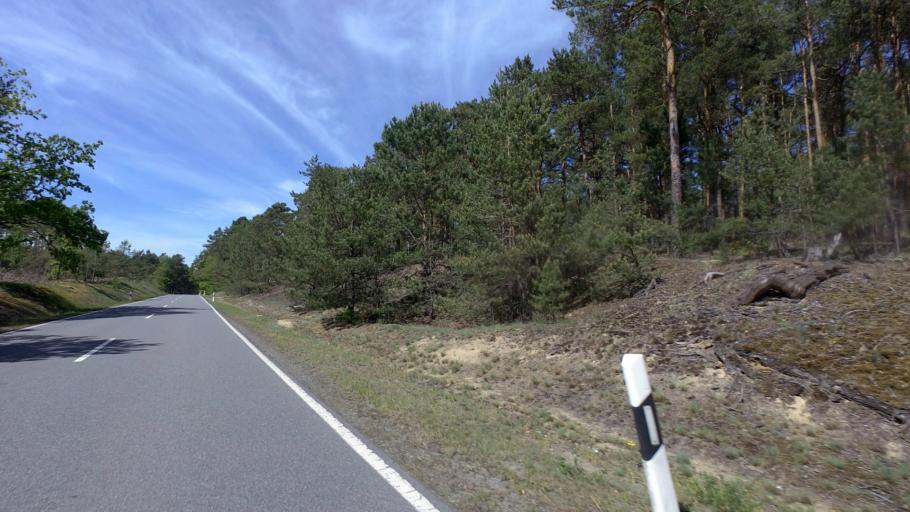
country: DE
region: Brandenburg
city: Sperenberg
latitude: 52.0894
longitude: 13.3910
